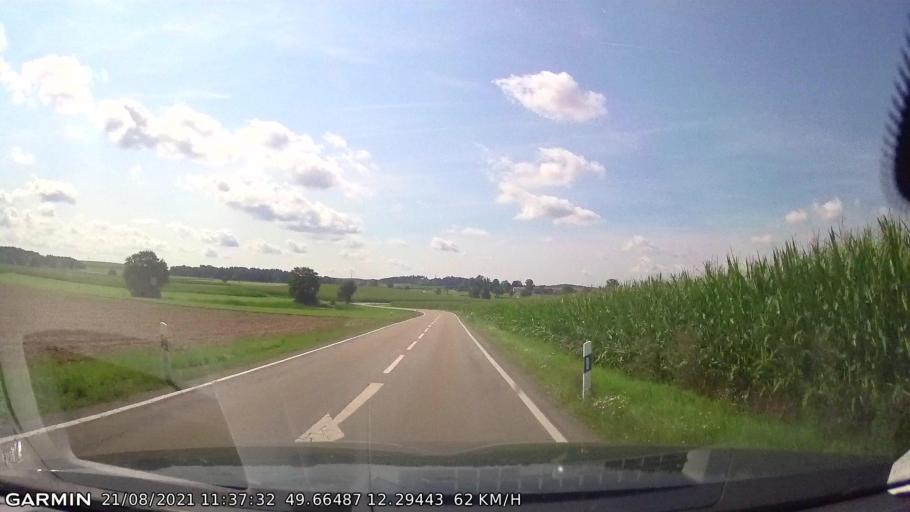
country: DE
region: Bavaria
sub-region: Upper Palatinate
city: Waldthurn
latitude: 49.6649
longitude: 12.2944
